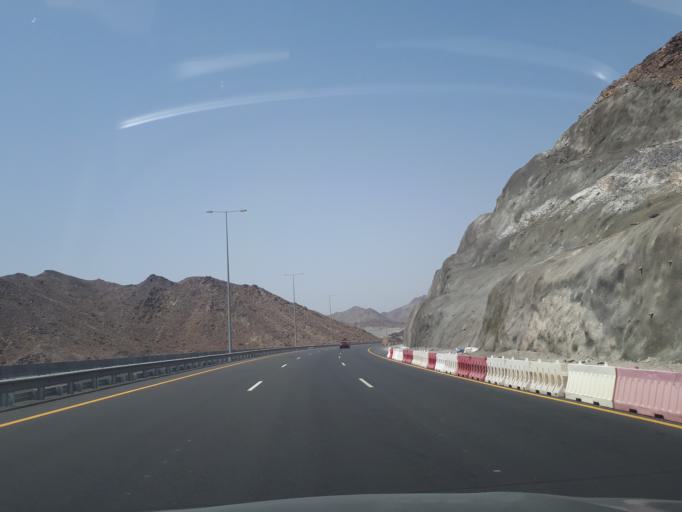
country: OM
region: Muhafazat ad Dakhiliyah
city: Bidbid
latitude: 23.3669
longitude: 58.1014
